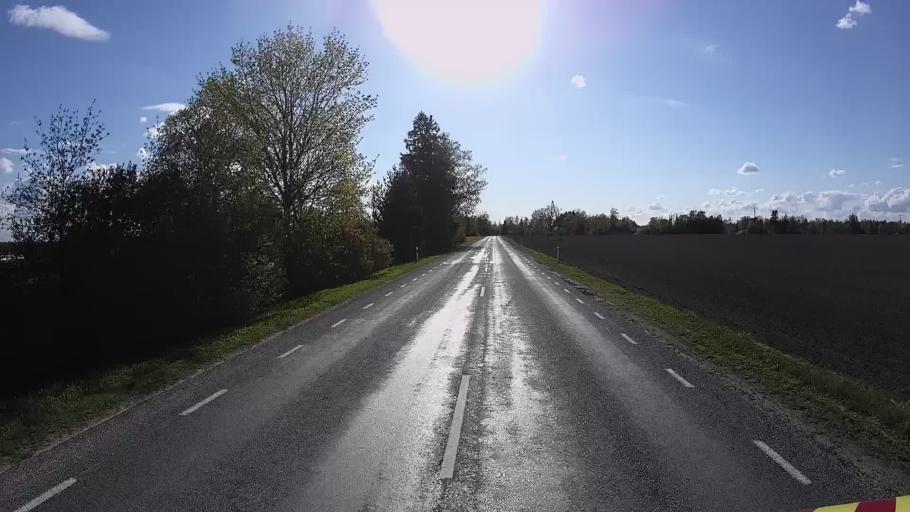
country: EE
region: Jogevamaa
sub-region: Poltsamaa linn
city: Poltsamaa
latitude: 58.6344
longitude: 25.8126
